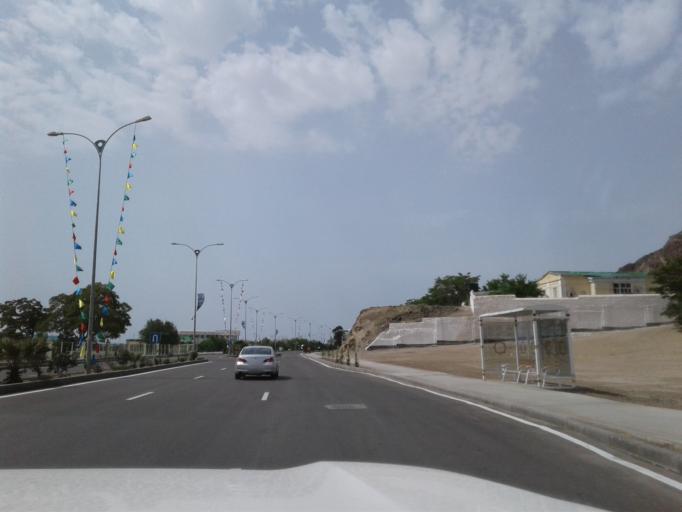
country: TM
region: Balkan
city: Turkmenbasy
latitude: 39.9970
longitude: 52.9920
